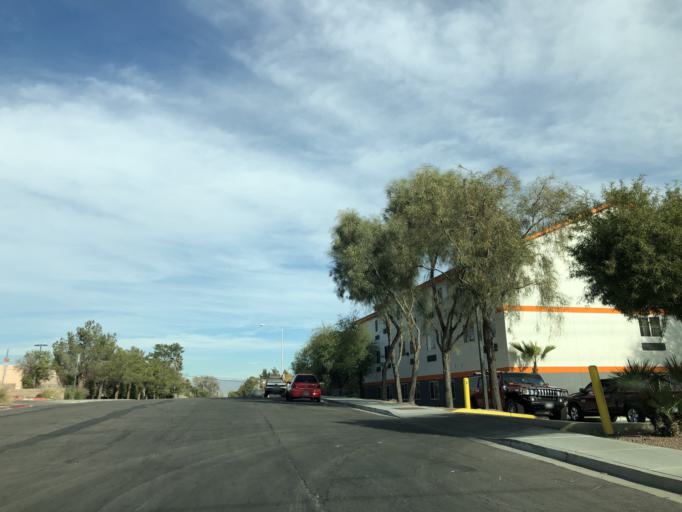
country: US
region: Nevada
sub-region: Clark County
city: Winchester
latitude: 36.1150
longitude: -115.1169
